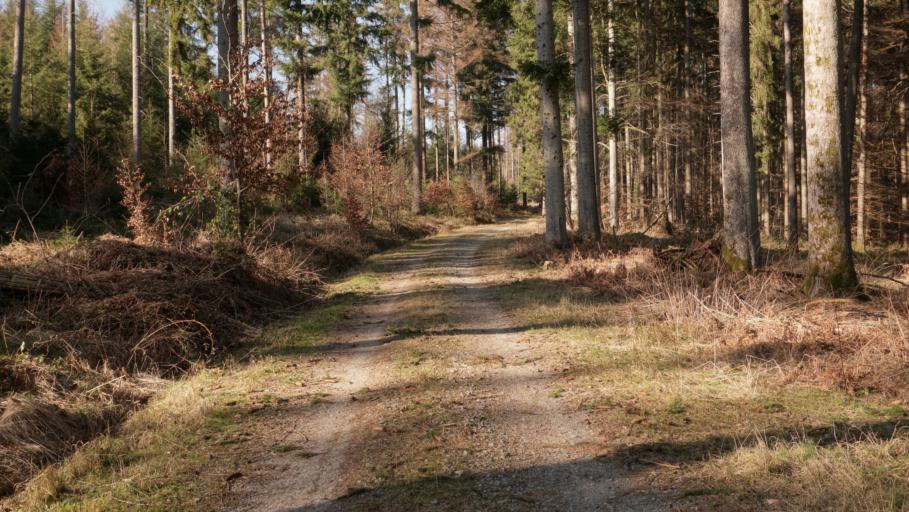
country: DE
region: Baden-Wuerttemberg
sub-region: Karlsruhe Region
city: Fahrenbach
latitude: 49.4459
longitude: 9.1471
